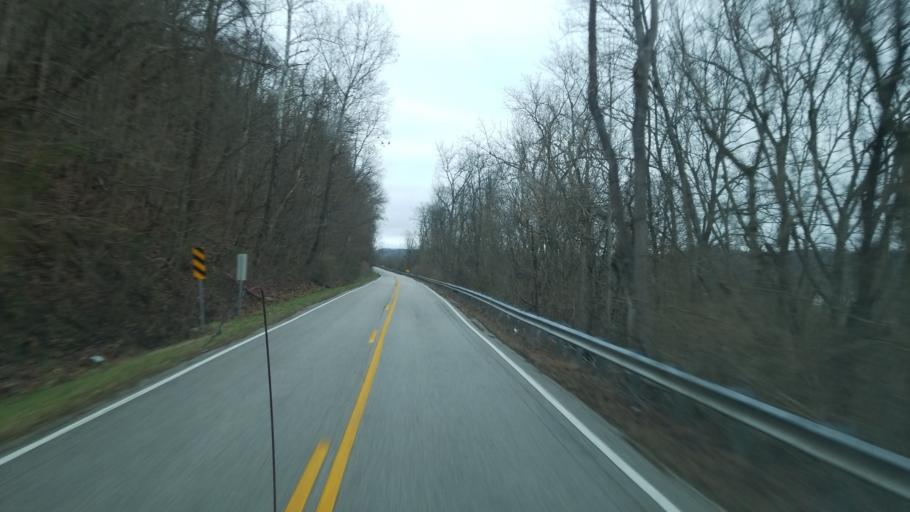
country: US
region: Kentucky
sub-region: Bracken County
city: Brooksville
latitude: 38.7815
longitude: -84.1355
